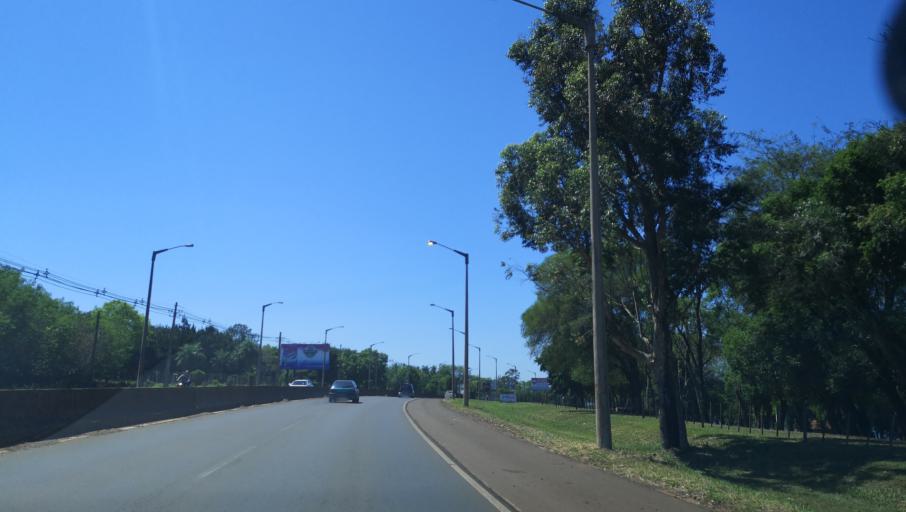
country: PY
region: Itapua
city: San Juan del Parana
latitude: -27.2917
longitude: -55.9160
